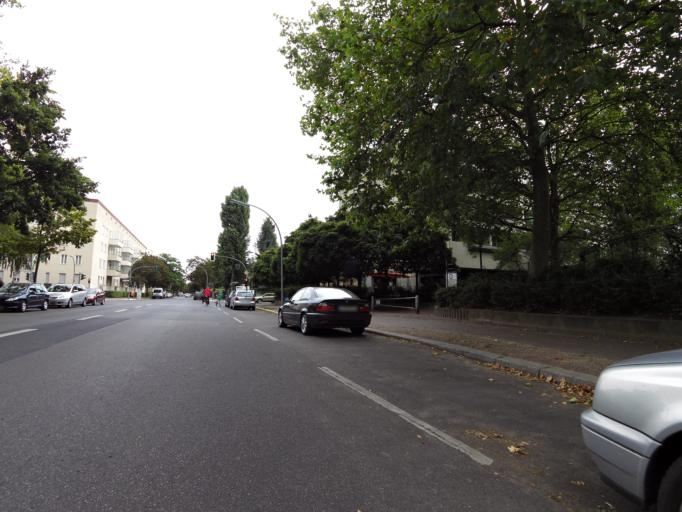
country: DE
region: Berlin
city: Wilmersdorf Bezirk
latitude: 52.4726
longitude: 13.3072
